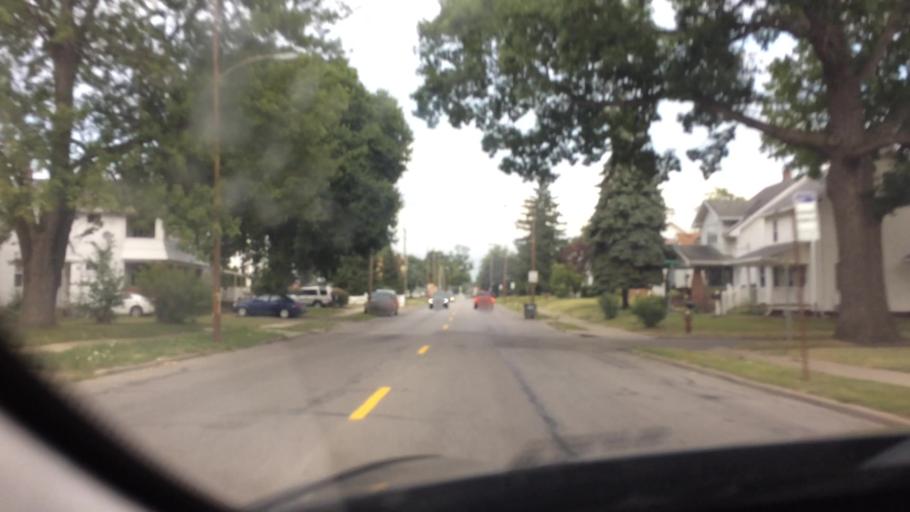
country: US
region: Ohio
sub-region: Wood County
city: Rossford
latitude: 41.6307
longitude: -83.5819
